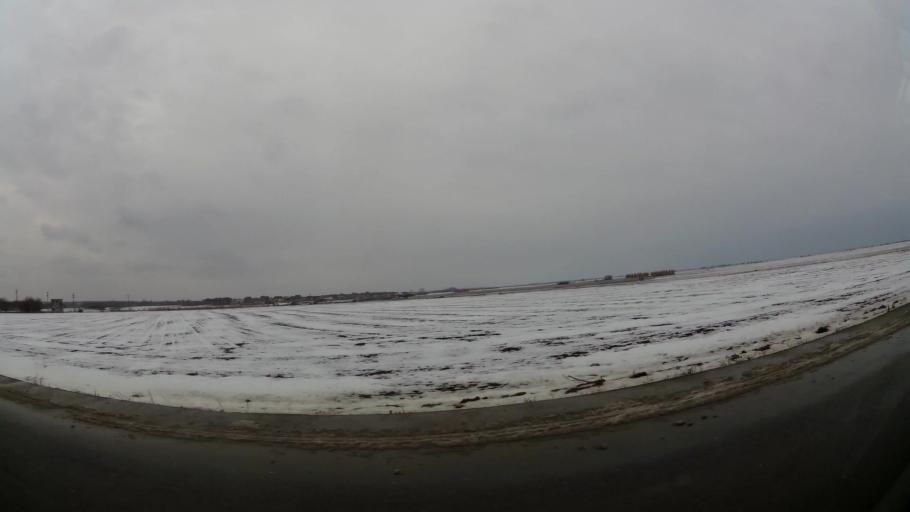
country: RO
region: Ilfov
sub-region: Comuna Tunari
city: Tunari
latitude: 44.5504
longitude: 26.1663
